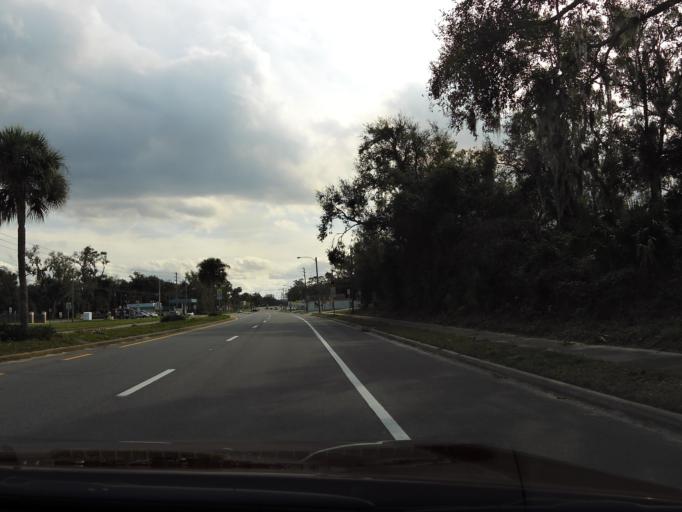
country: US
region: Florida
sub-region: Volusia County
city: De Leon Springs
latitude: 29.1236
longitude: -81.3519
